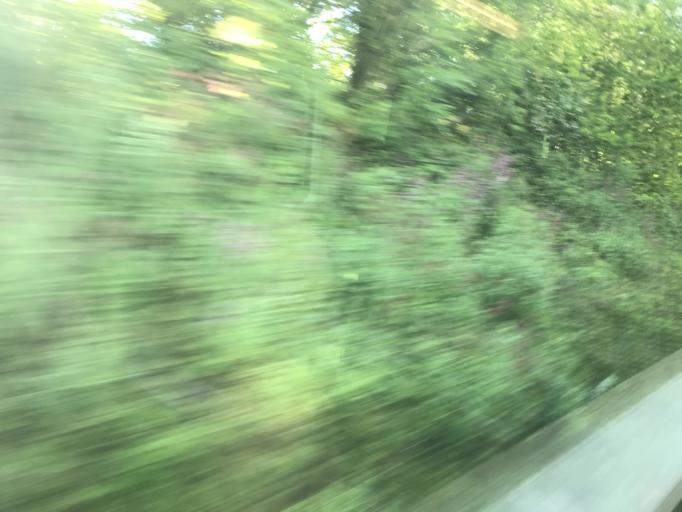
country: IE
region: Leinster
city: Shankill
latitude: 53.2402
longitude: -6.1176
